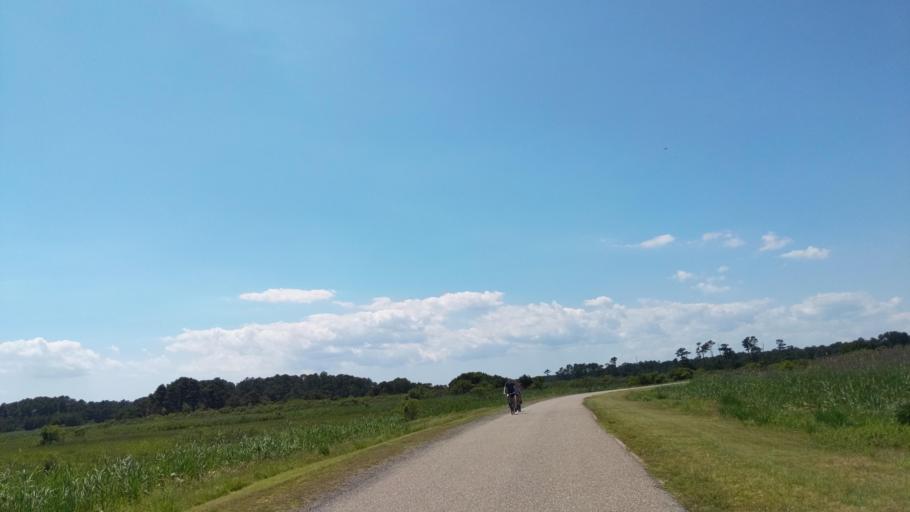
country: US
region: Virginia
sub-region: Accomack County
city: Chincoteague
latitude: 37.9020
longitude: -75.3483
